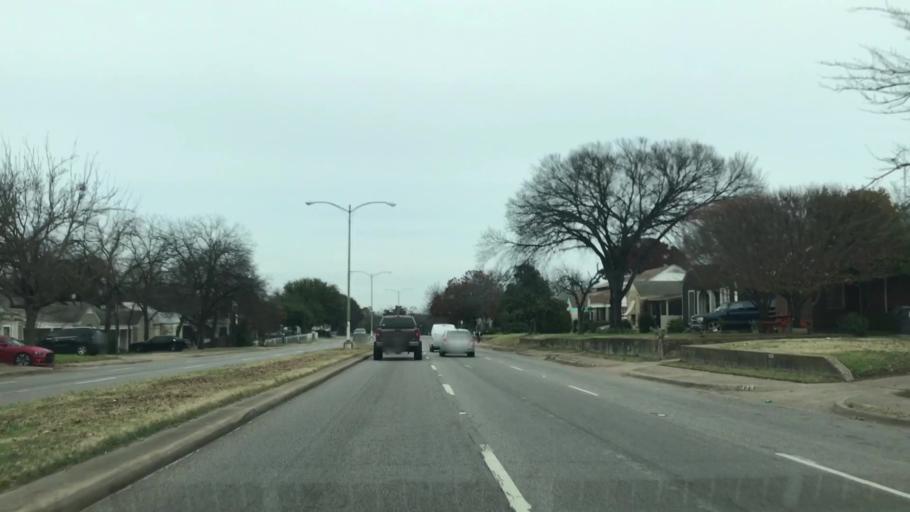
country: US
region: Texas
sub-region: Dallas County
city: Dallas
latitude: 32.7301
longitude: -96.8144
